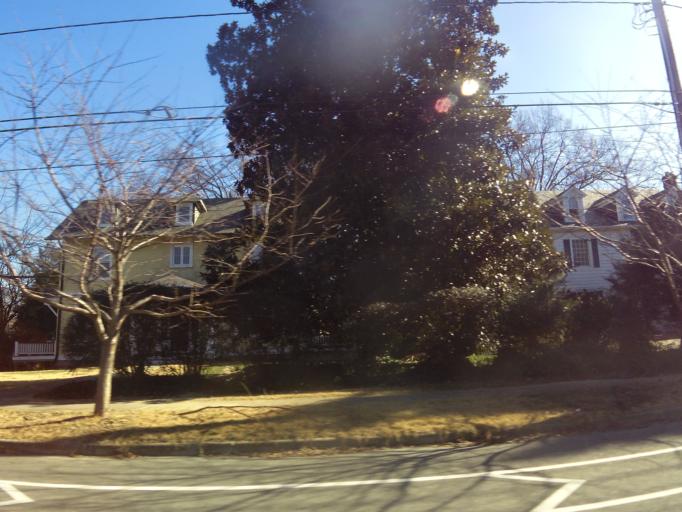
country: US
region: Virginia
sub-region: City of Richmond
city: Richmond
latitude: 37.5753
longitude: -77.4495
